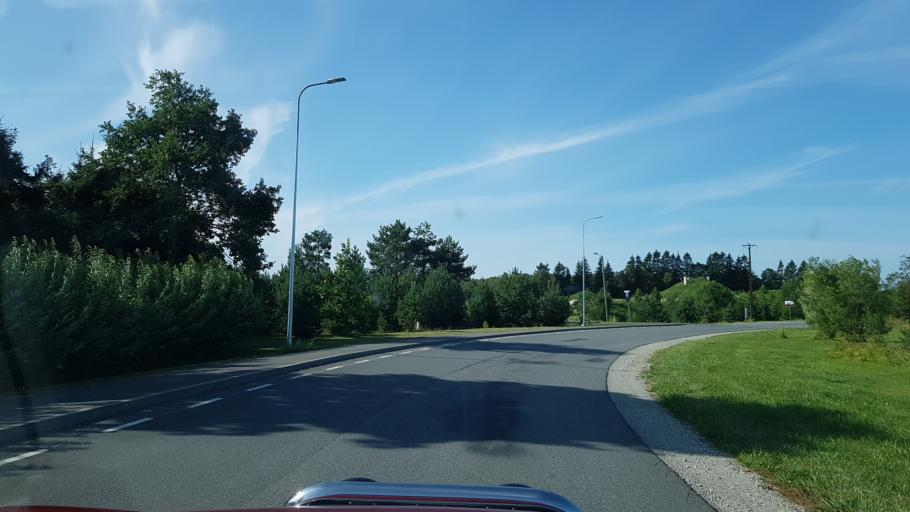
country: EE
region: Harju
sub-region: Rae vald
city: Jueri
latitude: 59.3848
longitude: 24.9333
